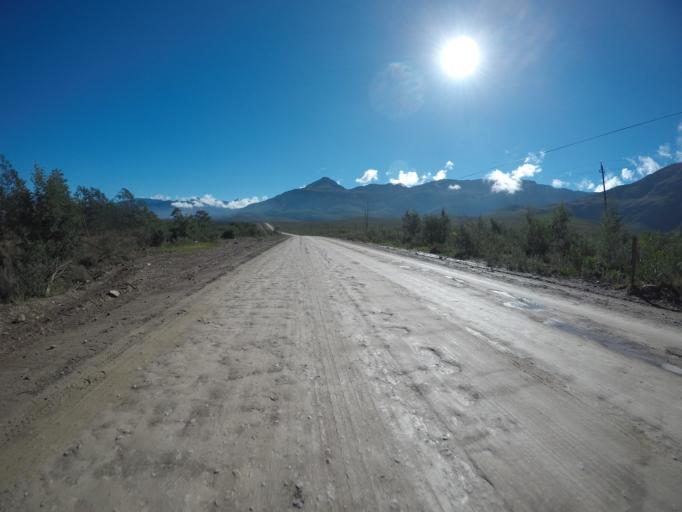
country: ZA
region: Western Cape
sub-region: Overberg District Municipality
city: Caledon
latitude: -34.0661
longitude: 19.6288
